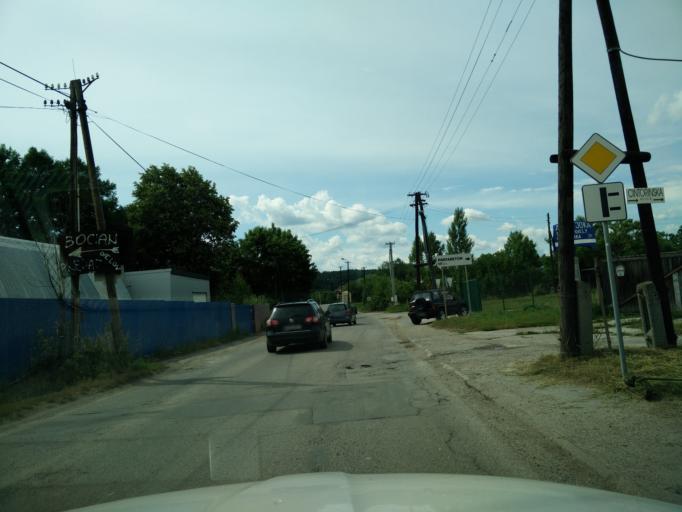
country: SK
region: Nitriansky
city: Bojnice
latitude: 48.7471
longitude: 18.5745
